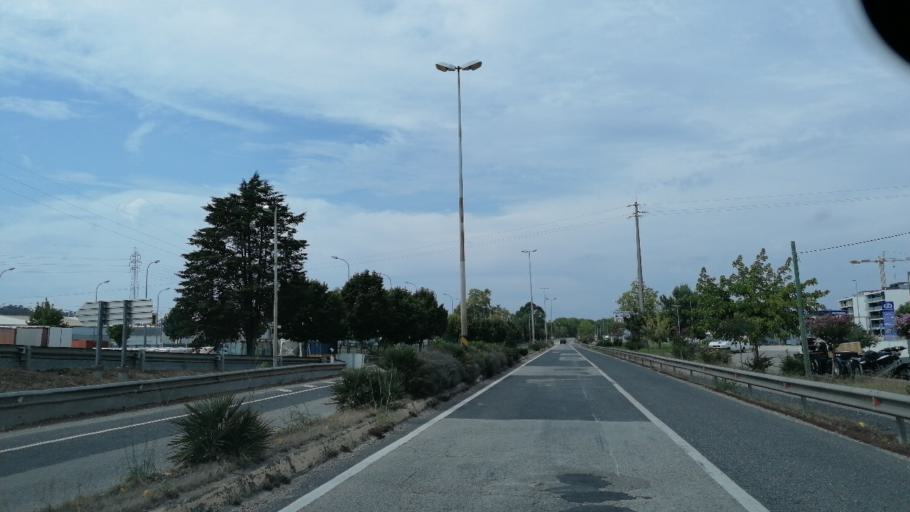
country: PT
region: Leiria
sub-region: Pombal
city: Pombal
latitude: 39.9150
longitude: -8.6332
